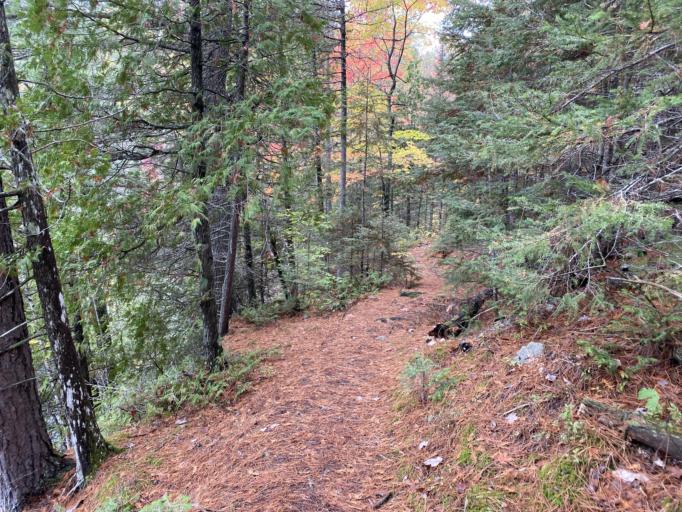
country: US
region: Michigan
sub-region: Marquette County
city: West Ishpeming
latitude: 46.5407
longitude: -87.9993
